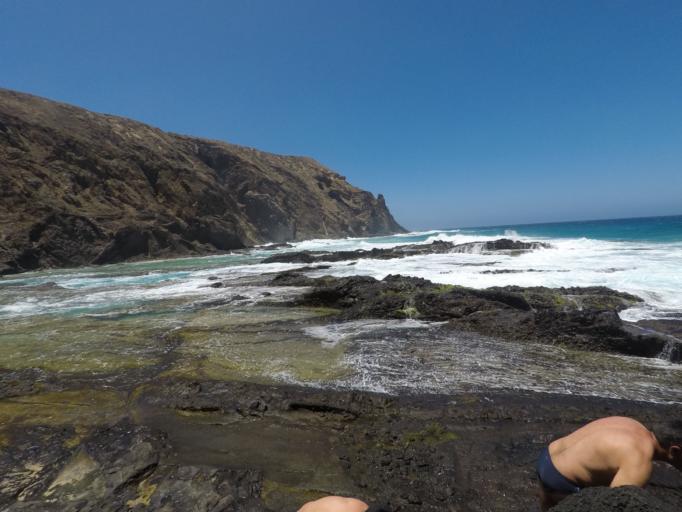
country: PT
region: Madeira
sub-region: Porto Santo
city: Camacha
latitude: 33.0935
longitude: -16.3474
